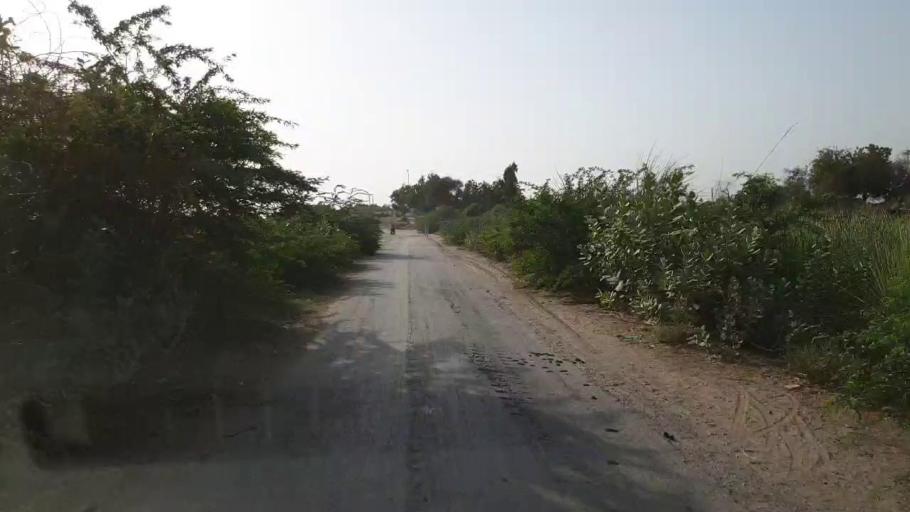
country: PK
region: Sindh
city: Jam Sahib
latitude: 26.4339
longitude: 68.8754
